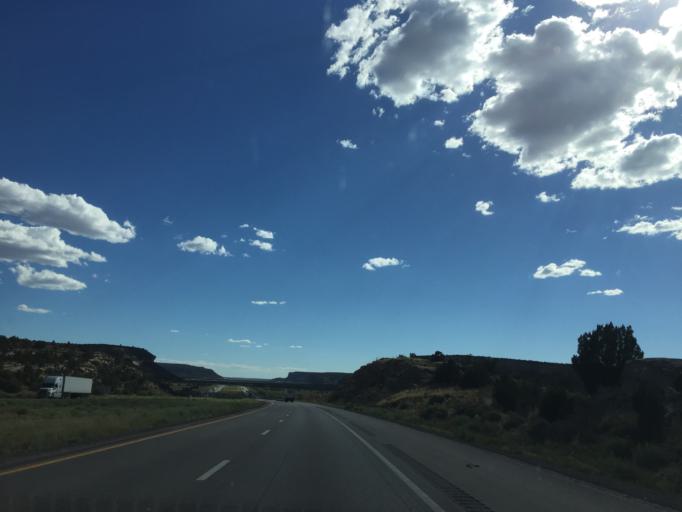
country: US
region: Arizona
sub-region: Apache County
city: Saint Michaels
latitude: 35.4221
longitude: -108.9881
